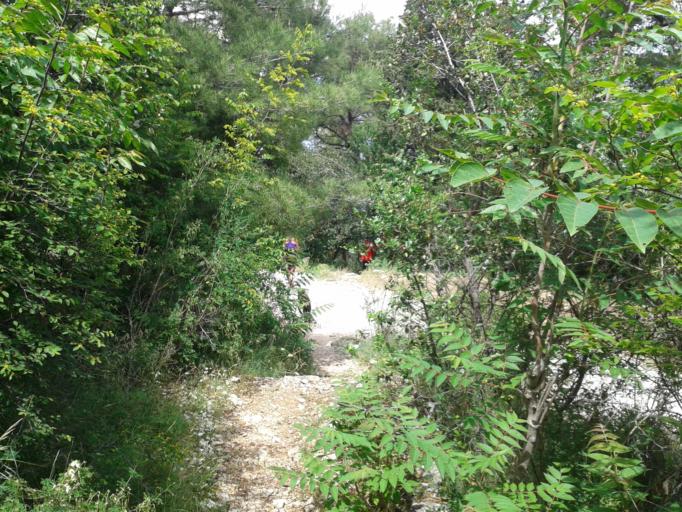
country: HR
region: Splitsko-Dalmatinska
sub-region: Grad Split
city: Split
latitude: 43.5118
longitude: 16.4202
